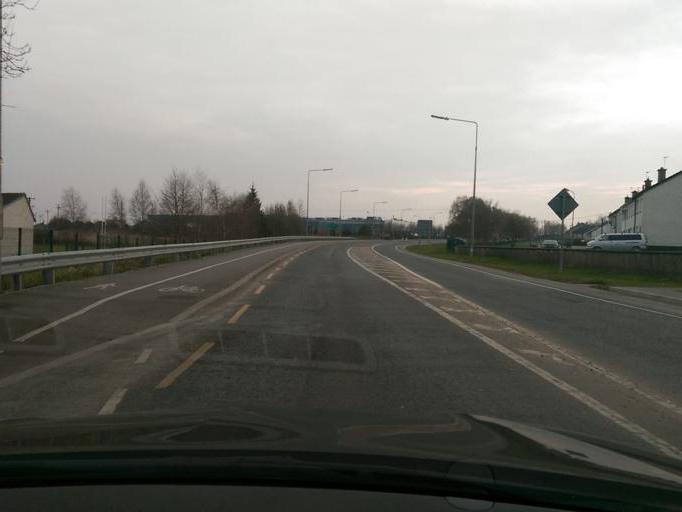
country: IE
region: Leinster
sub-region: An Iarmhi
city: Athlone
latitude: 53.4354
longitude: -7.9031
